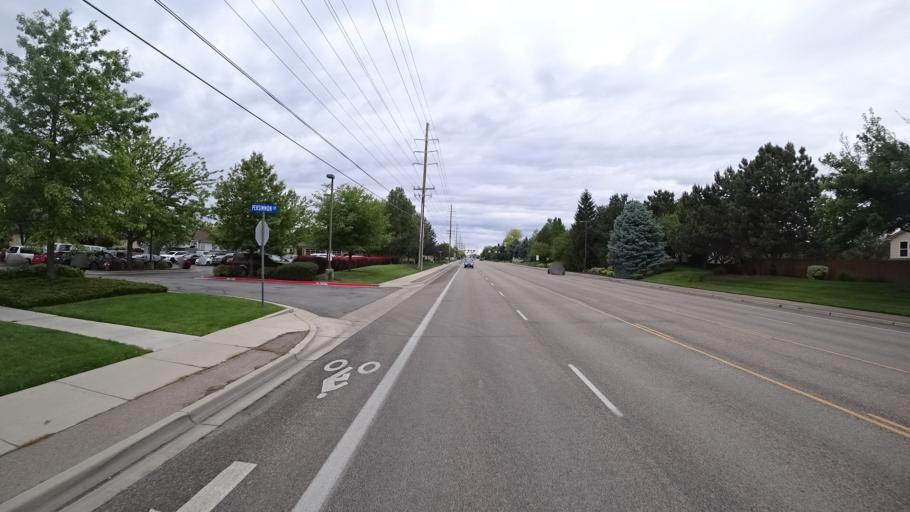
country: US
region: Idaho
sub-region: Ada County
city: Eagle
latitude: 43.6484
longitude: -116.3448
